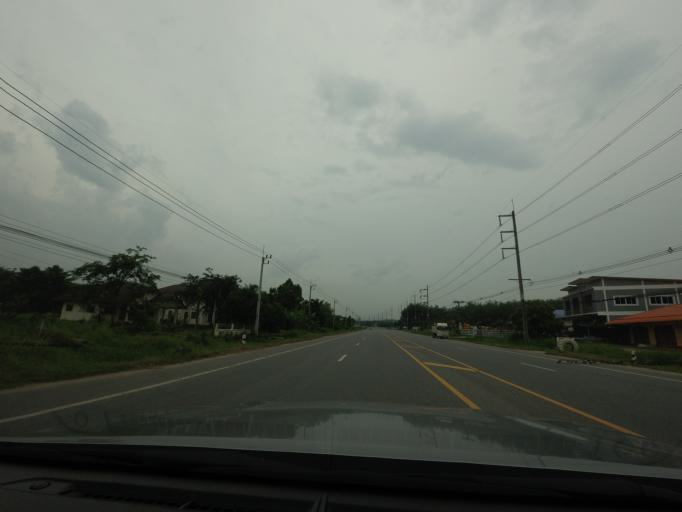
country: TH
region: Songkhla
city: Na Mom
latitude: 7.0489
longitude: 100.6527
